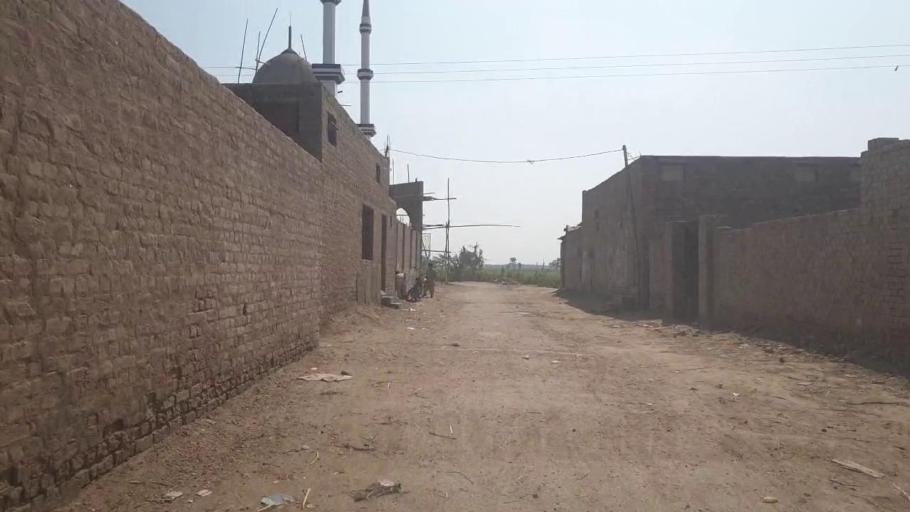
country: PK
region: Sindh
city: Mirpur Khas
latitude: 25.4892
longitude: 68.8895
